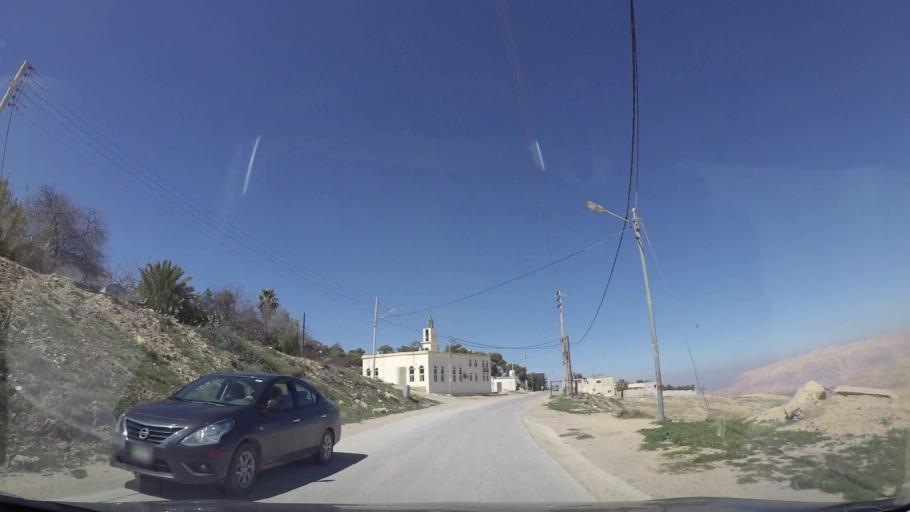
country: JO
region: Tafielah
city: At Tafilah
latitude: 30.8403
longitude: 35.5692
